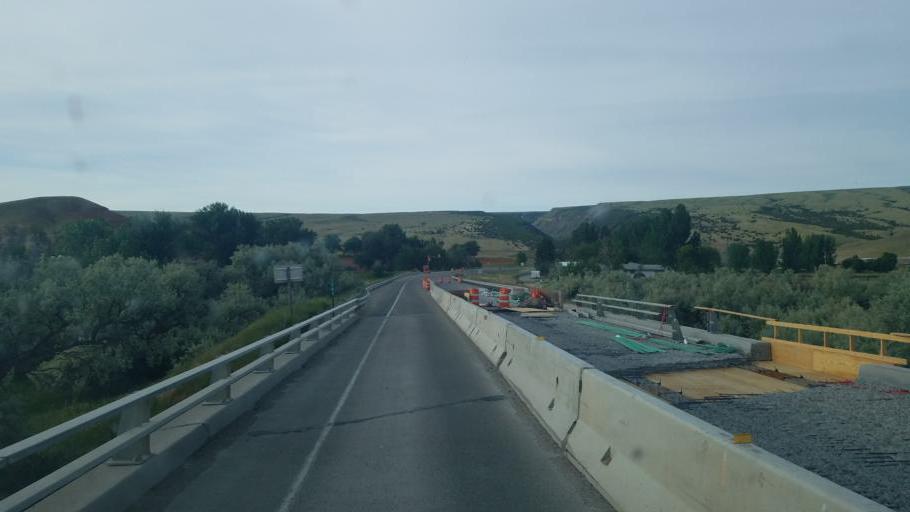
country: US
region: Wyoming
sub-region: Hot Springs County
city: Thermopolis
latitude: 43.5925
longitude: -108.2137
